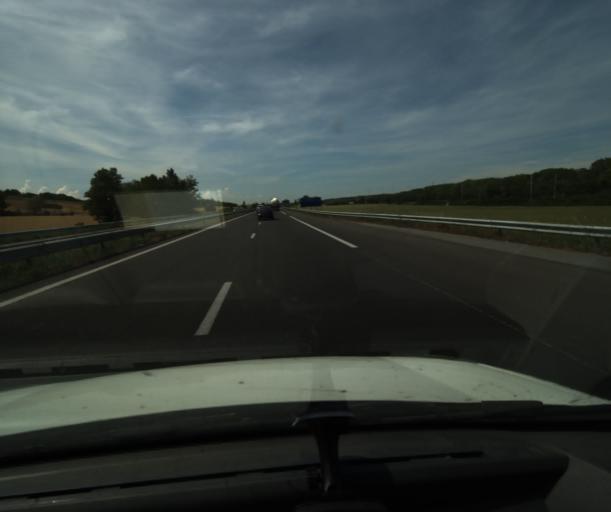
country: FR
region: Midi-Pyrenees
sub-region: Departement de la Haute-Garonne
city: Avignonet-Lauragais
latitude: 43.3425
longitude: 1.8259
